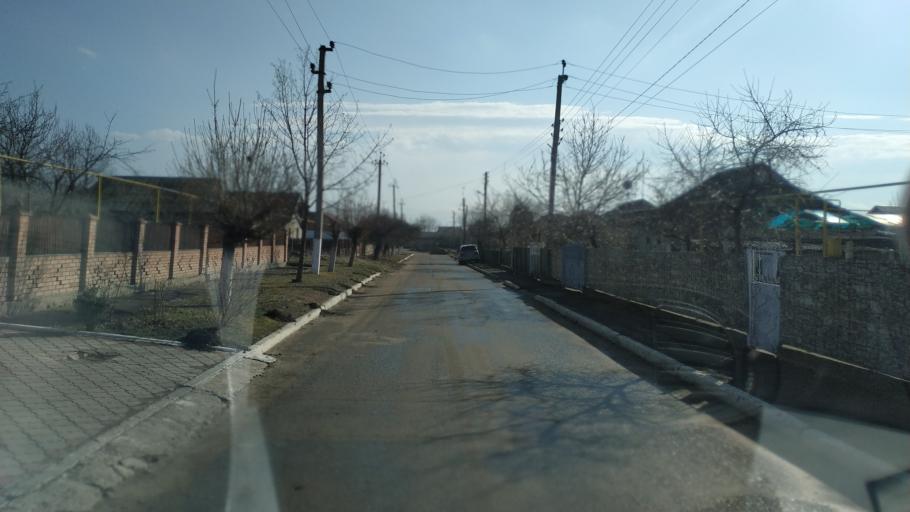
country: MD
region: Chisinau
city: Singera
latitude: 46.6839
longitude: 29.0614
